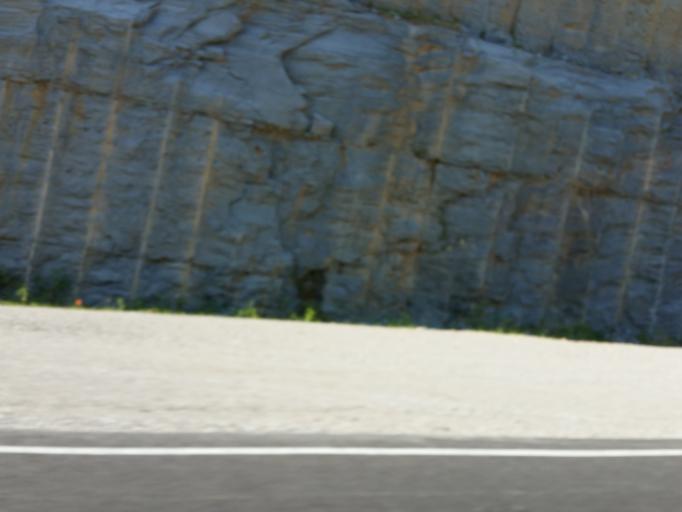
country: US
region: Tennessee
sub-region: Maury County
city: Mount Pleasant
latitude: 35.5688
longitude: -87.3356
